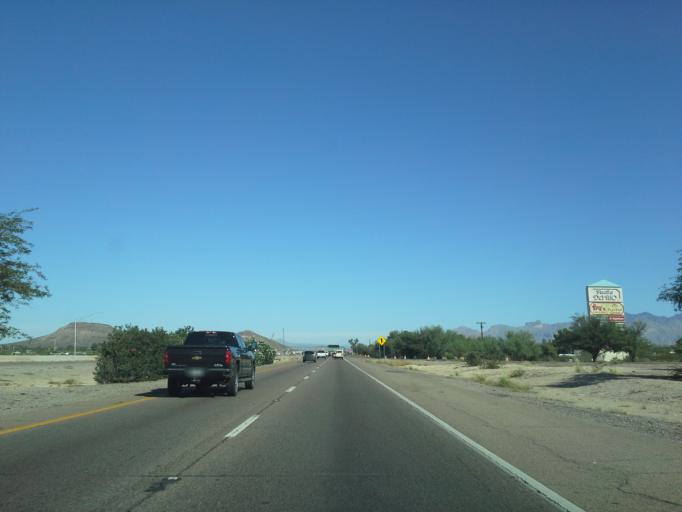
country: US
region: Arizona
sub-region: Pima County
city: South Tucson
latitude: 32.1654
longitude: -110.9854
